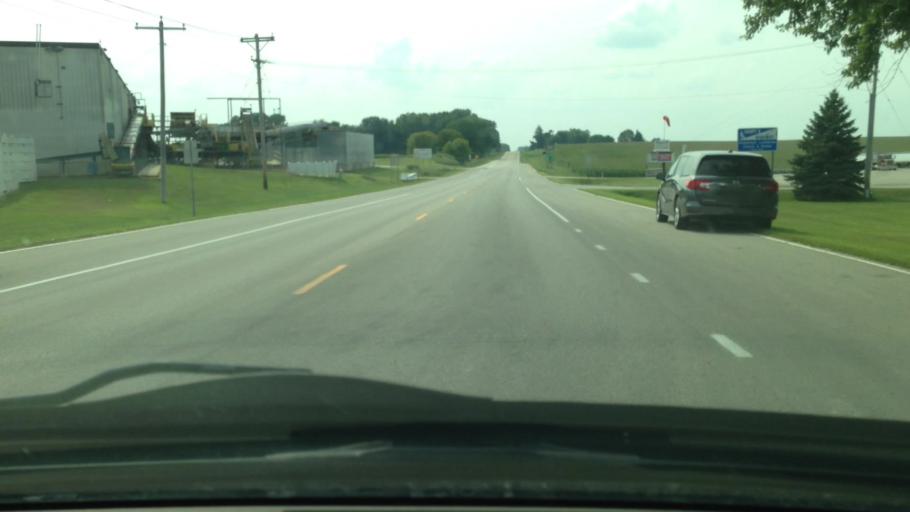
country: US
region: Minnesota
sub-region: Wabasha County
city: Plainview
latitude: 44.1649
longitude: -92.1803
